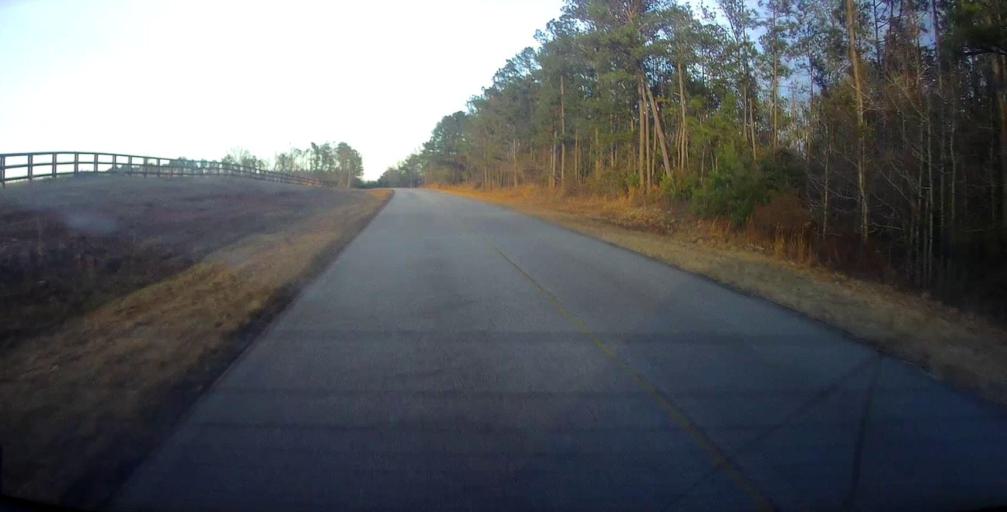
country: US
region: Georgia
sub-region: Harris County
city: Hamilton
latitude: 32.6071
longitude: -84.8703
